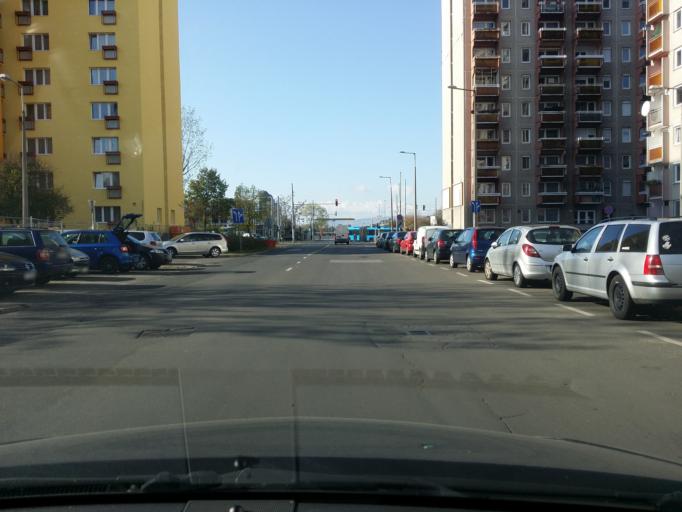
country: HU
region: Budapest
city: Budapest X. keruelet
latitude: 47.5013
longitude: 19.1385
